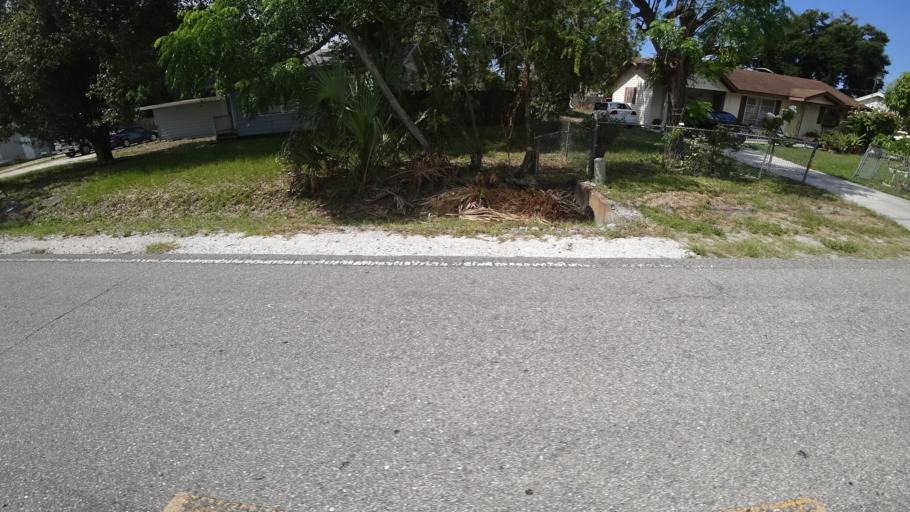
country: US
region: Florida
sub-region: Manatee County
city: West Samoset
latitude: 27.4514
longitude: -82.5510
